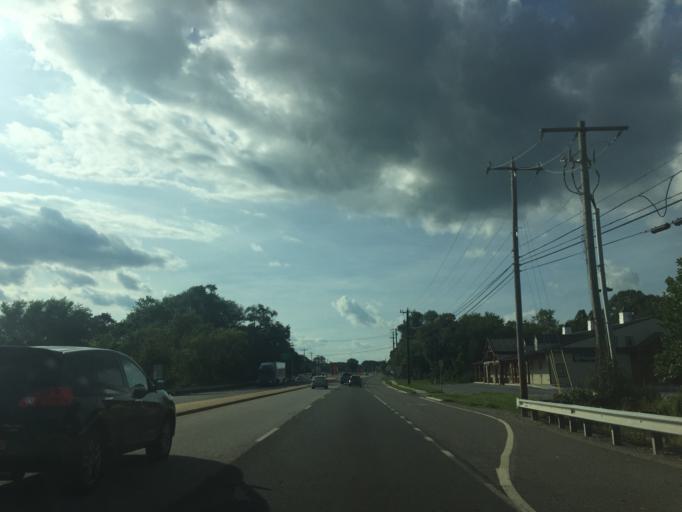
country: US
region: Delaware
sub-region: Kent County
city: Smyrna
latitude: 39.3088
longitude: -75.6092
